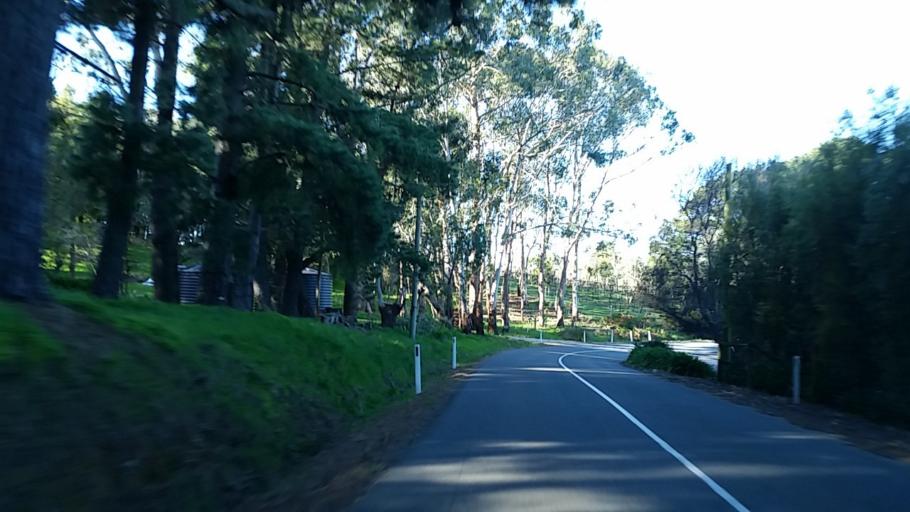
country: AU
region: South Australia
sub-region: Adelaide Hills
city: Adelaide Hills
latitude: -34.9458
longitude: 138.7239
